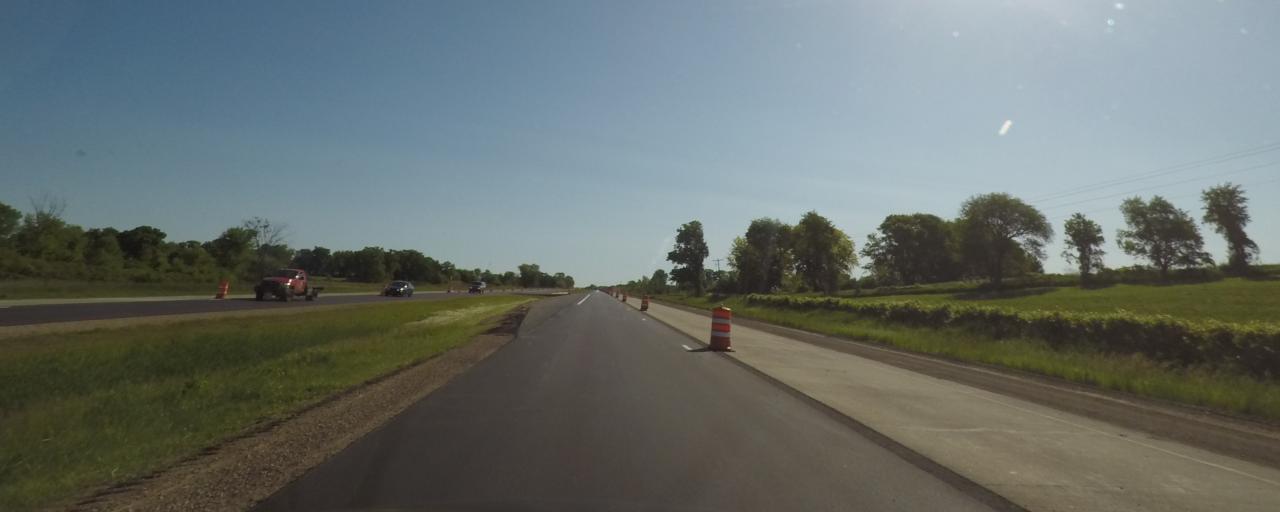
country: US
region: Wisconsin
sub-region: Columbia County
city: Columbus
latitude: 43.3823
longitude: -88.9556
